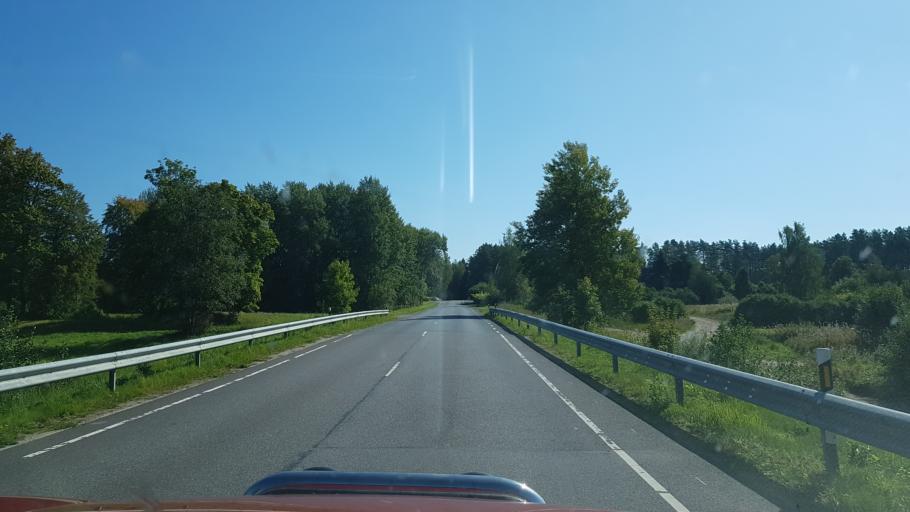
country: EE
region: Polvamaa
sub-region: Polva linn
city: Polva
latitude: 58.2689
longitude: 27.1320
